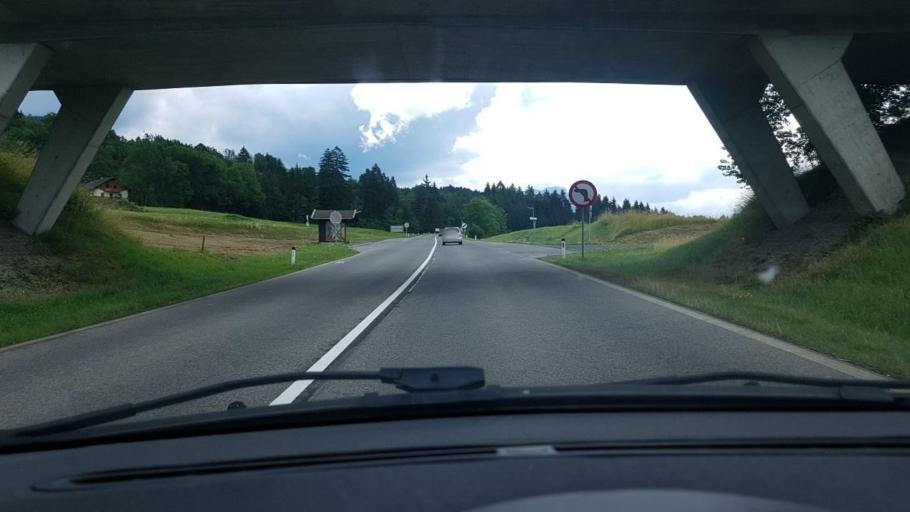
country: AT
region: Carinthia
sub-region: Politischer Bezirk Villach Land
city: Stockenboi
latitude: 46.6224
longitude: 13.4930
